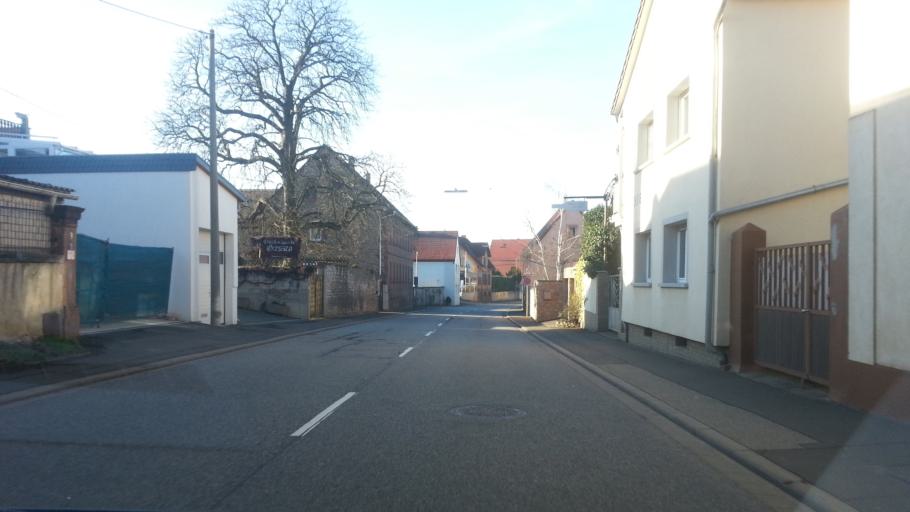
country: DE
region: Rheinland-Pfalz
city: Molsheim
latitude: 49.6364
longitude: 8.1666
